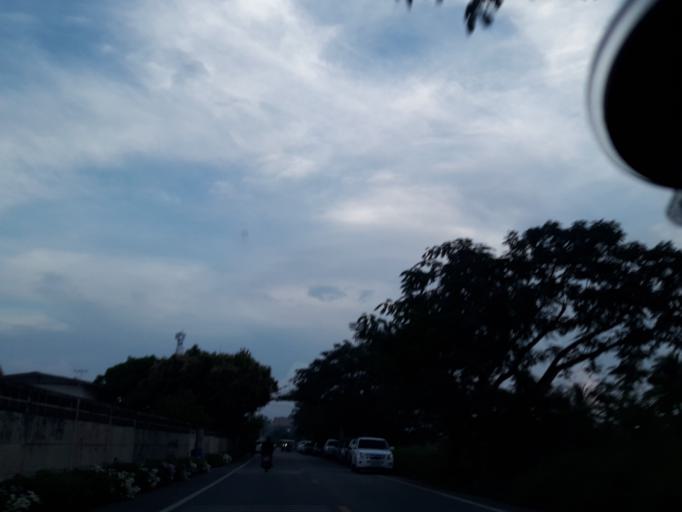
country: TH
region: Pathum Thani
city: Nong Suea
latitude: 14.1380
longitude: 100.8690
